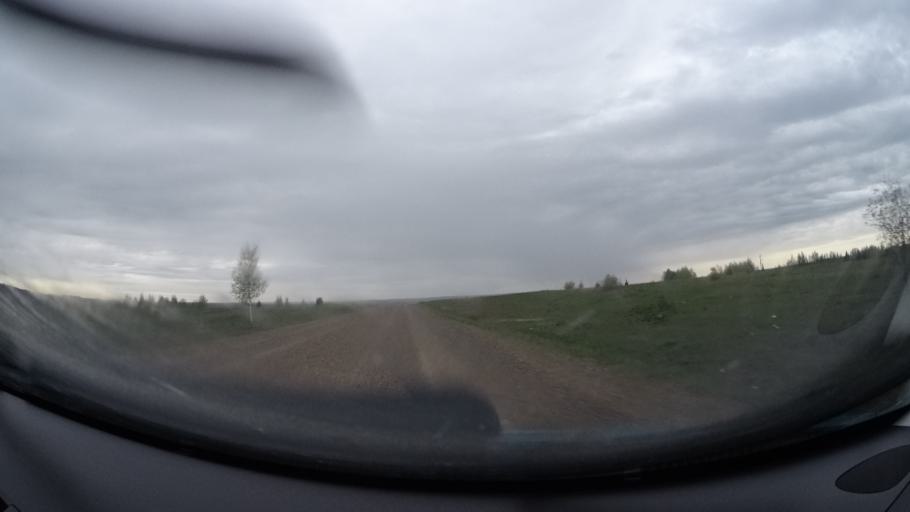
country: RU
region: Perm
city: Kuyeda
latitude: 56.5705
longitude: 55.6833
